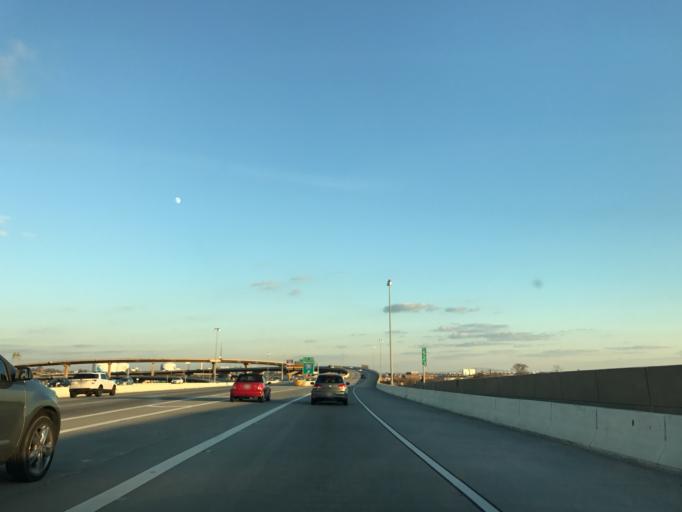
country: US
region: Maryland
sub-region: City of Baltimore
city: Baltimore
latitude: 39.2687
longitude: -76.6308
